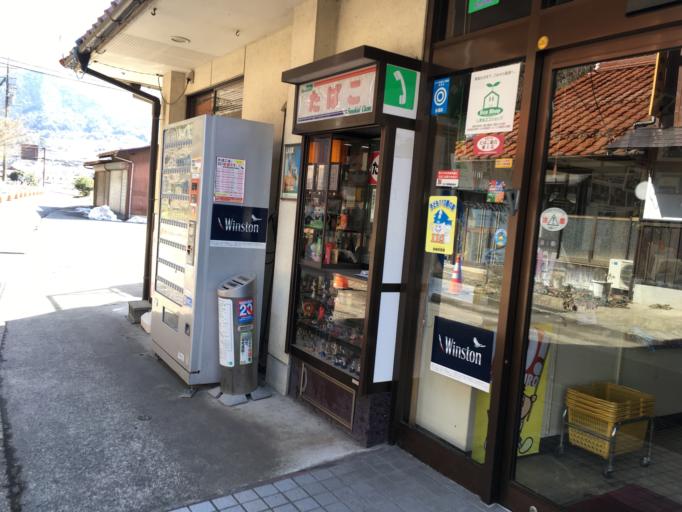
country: JP
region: Shimane
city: Masuda
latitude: 34.4526
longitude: 131.7587
